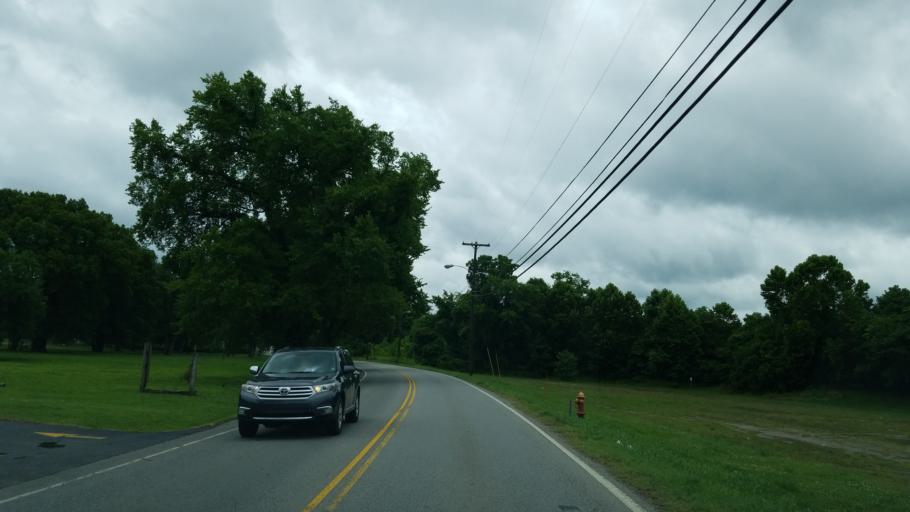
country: US
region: Tennessee
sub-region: Rutherford County
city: La Vergne
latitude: 36.0618
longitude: -86.6762
